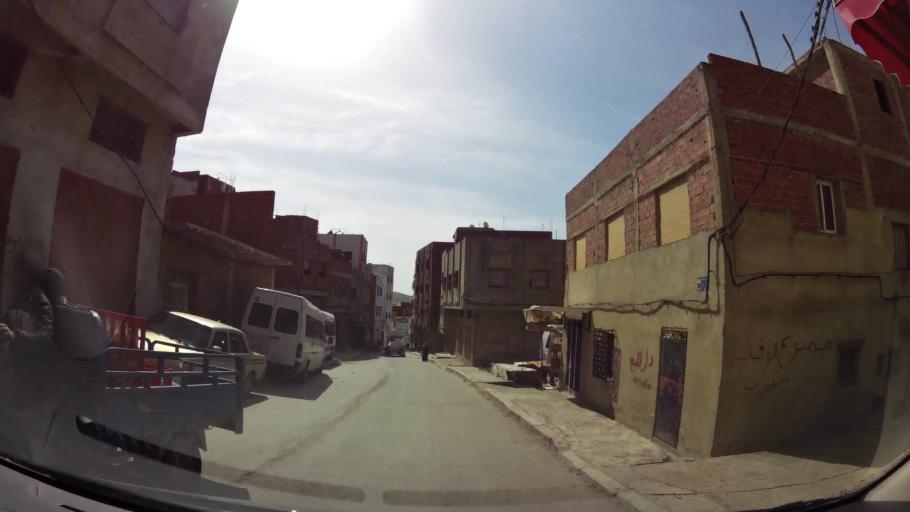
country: MA
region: Tanger-Tetouan
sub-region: Tanger-Assilah
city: Tangier
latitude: 35.7296
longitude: -5.8126
